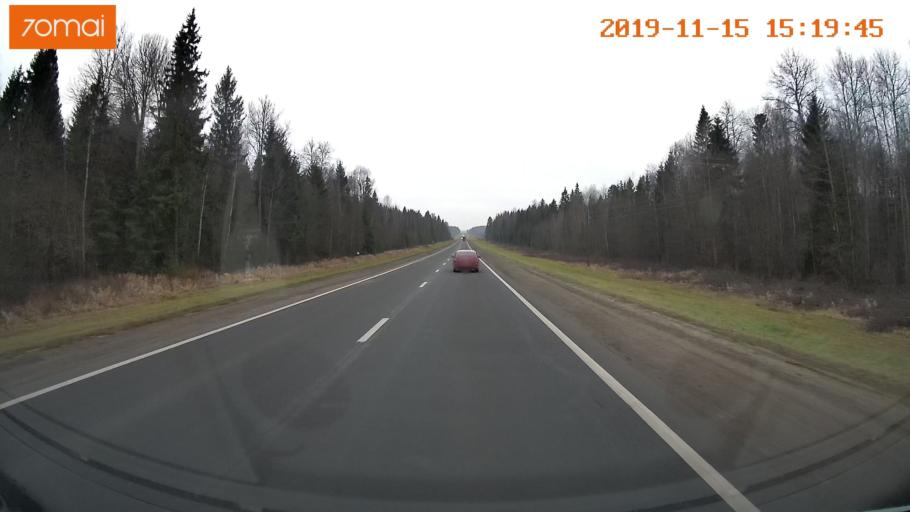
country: RU
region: Jaroslavl
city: Danilov
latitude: 58.2309
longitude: 40.1726
